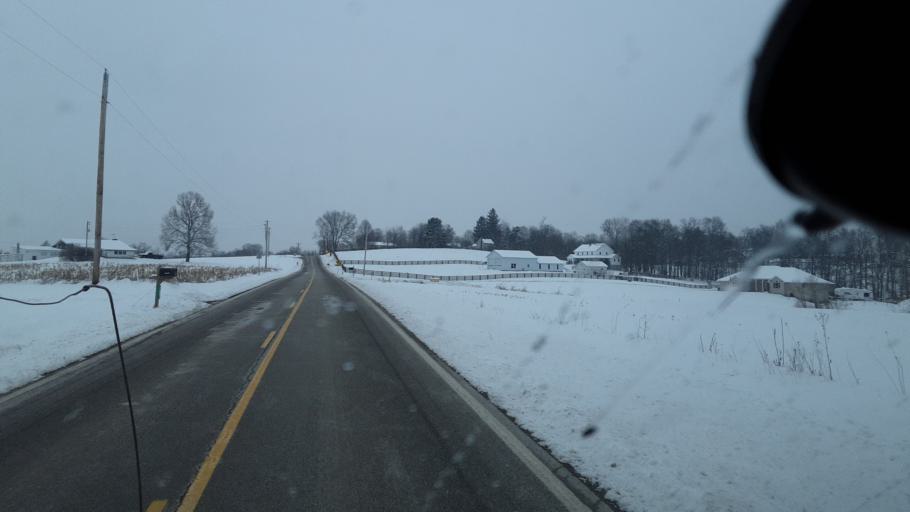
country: US
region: Ohio
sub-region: Perry County
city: Somerset
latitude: 39.8585
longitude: -82.2514
